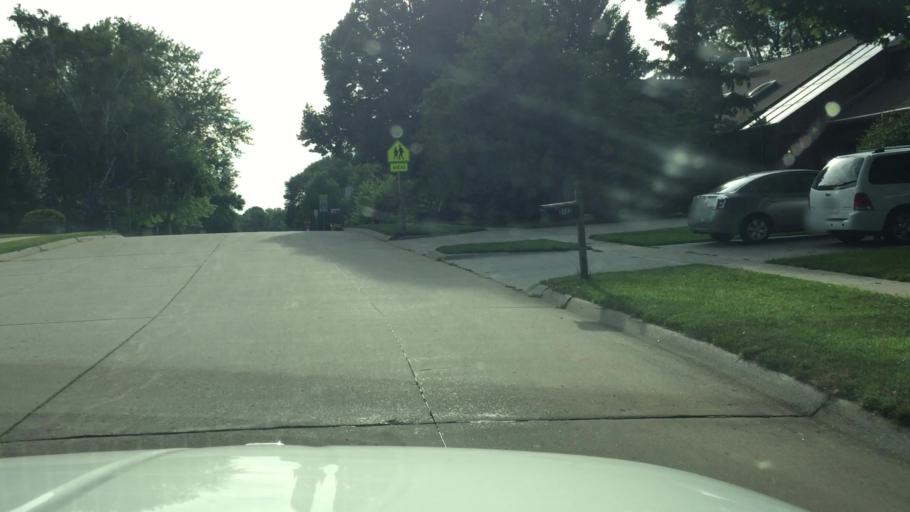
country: US
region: Iowa
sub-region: Johnson County
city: Iowa City
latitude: 41.6611
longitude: -91.4869
